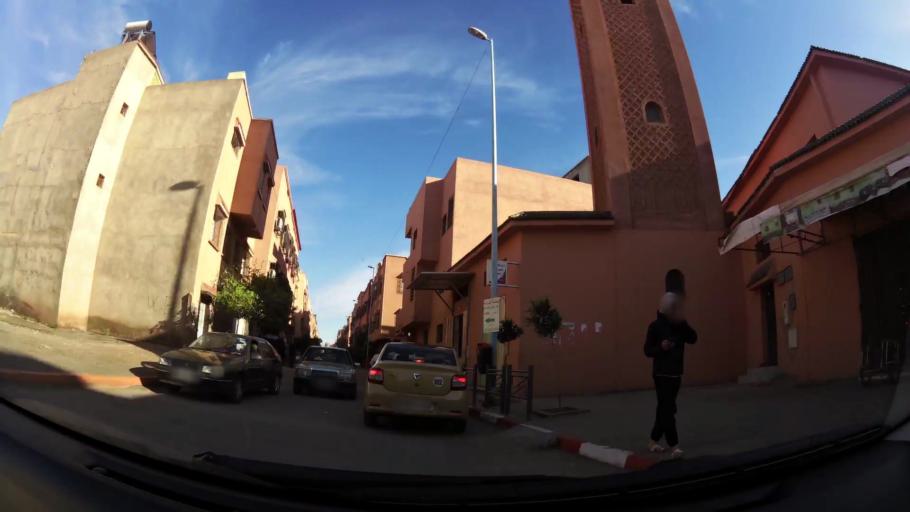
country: MA
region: Marrakech-Tensift-Al Haouz
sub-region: Marrakech
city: Marrakesh
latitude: 31.6224
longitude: -8.0691
